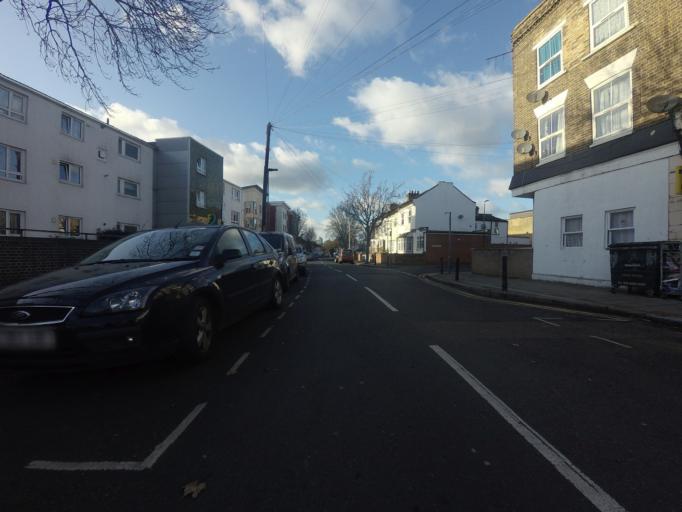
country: GB
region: England
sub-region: Greater London
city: East Ham
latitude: 51.5337
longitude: 0.0186
